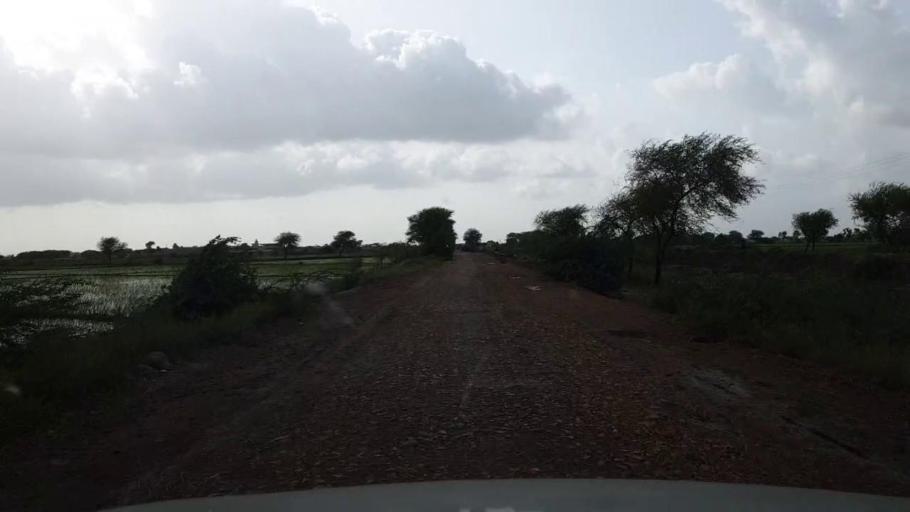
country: PK
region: Sindh
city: Kario
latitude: 24.7697
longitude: 68.5973
